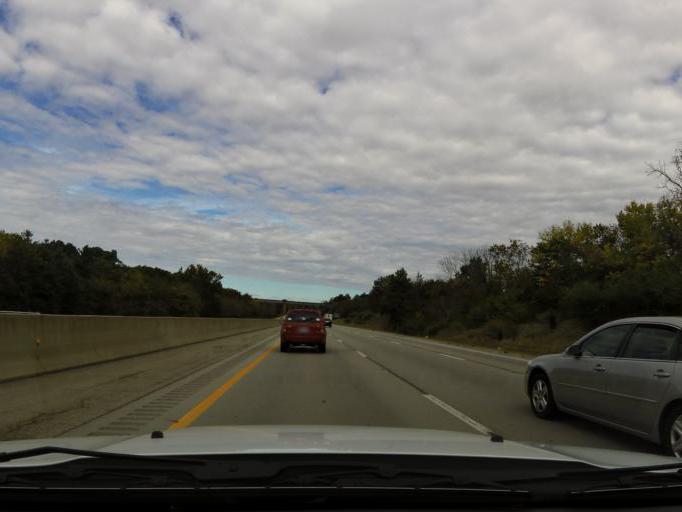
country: US
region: Kentucky
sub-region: Boone County
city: Walton
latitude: 38.8371
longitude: -84.6110
